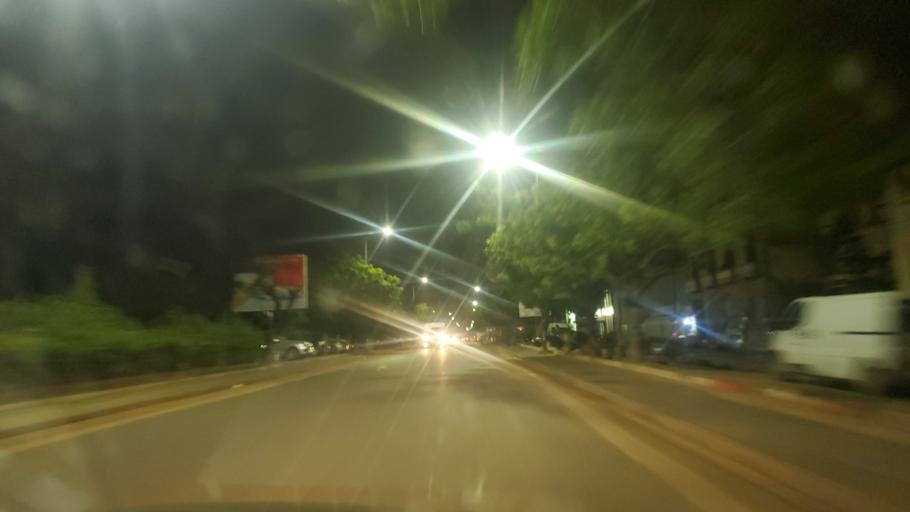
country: SN
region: Dakar
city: Grand Dakar
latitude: 14.7080
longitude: -17.4593
